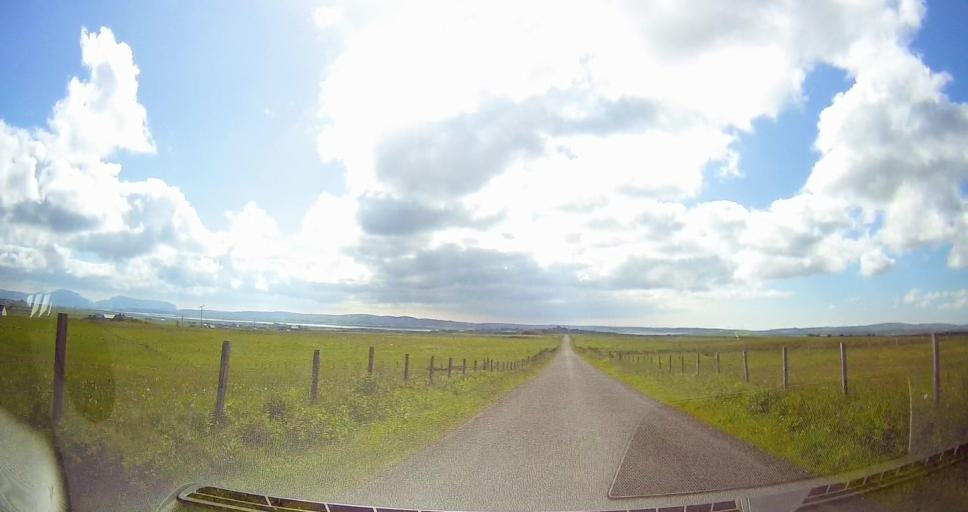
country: GB
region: Scotland
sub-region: Orkney Islands
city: Stromness
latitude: 59.0454
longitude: -3.1659
